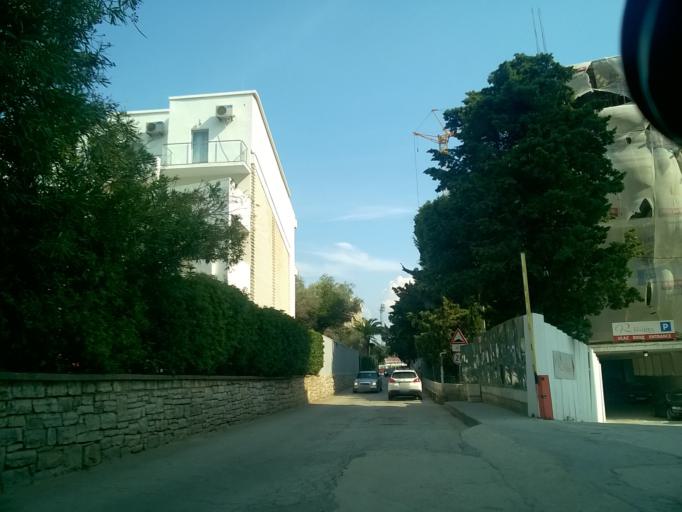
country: ME
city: Petrovac na Moru
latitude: 42.2049
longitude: 18.9443
